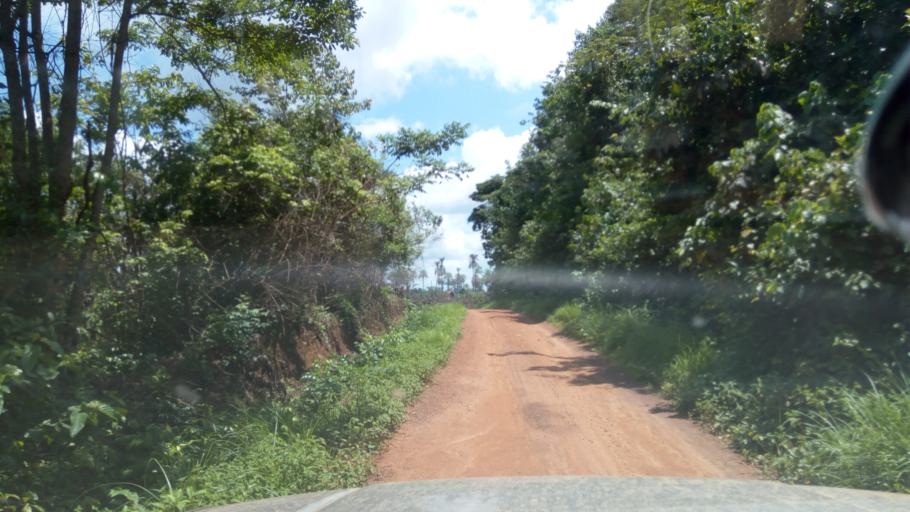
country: SL
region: Southern Province
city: Zimmi
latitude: 7.3070
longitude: -11.2955
